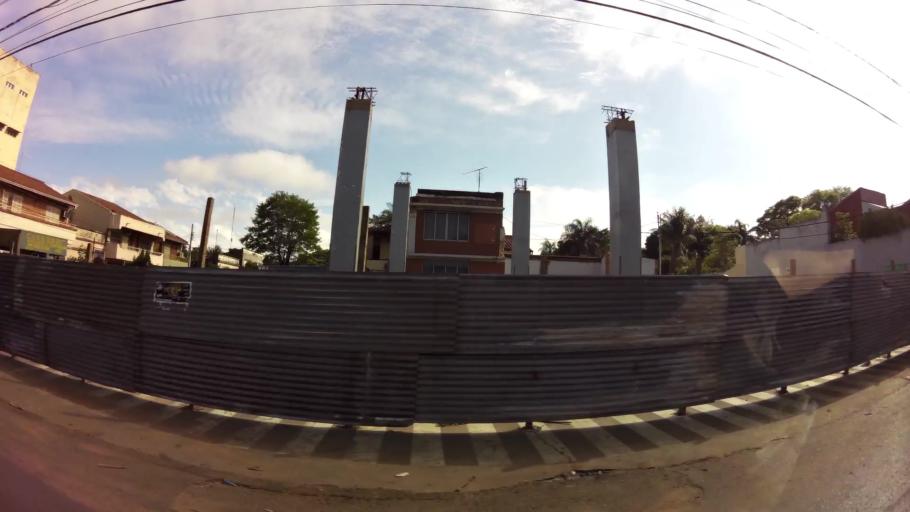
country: PY
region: Central
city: San Lorenzo
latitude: -25.2665
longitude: -57.4959
